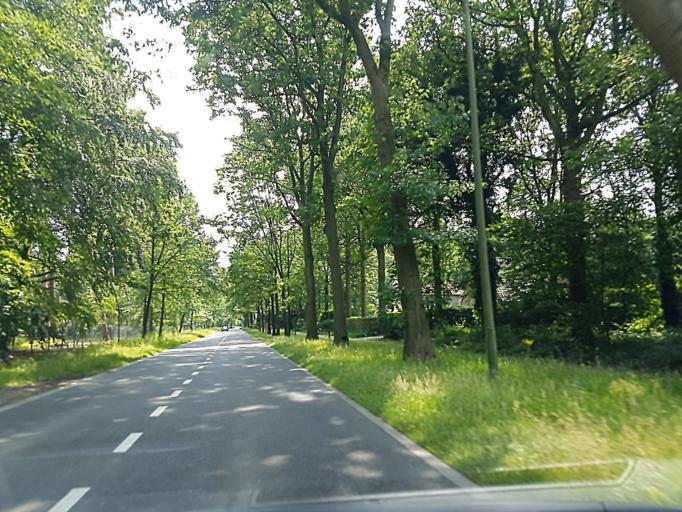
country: BE
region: Flanders
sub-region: Provincie Antwerpen
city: Wijnegem
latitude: 51.2459
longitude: 4.5402
